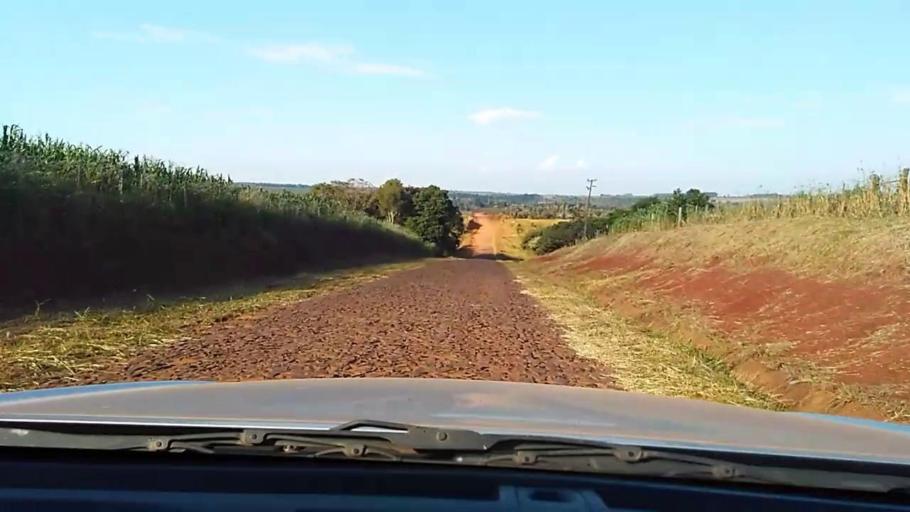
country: PY
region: Alto Parana
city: Doctor Juan Leon Mallorquin
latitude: -25.6981
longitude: -55.3808
